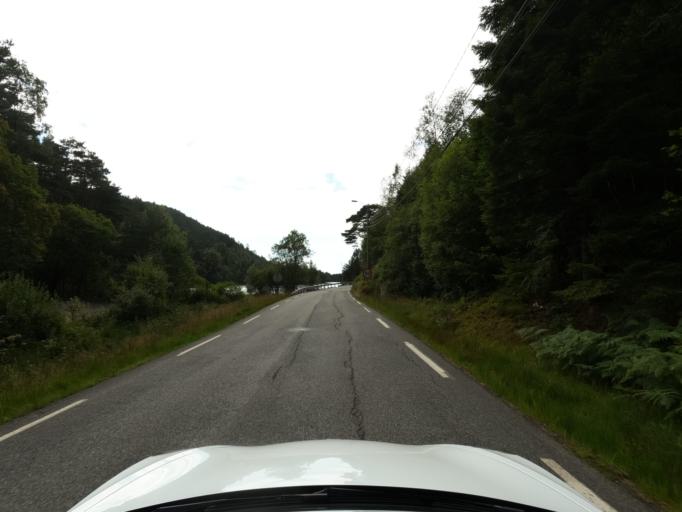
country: NO
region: Hordaland
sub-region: Os
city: Hagavik
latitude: 60.1993
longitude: 5.3729
